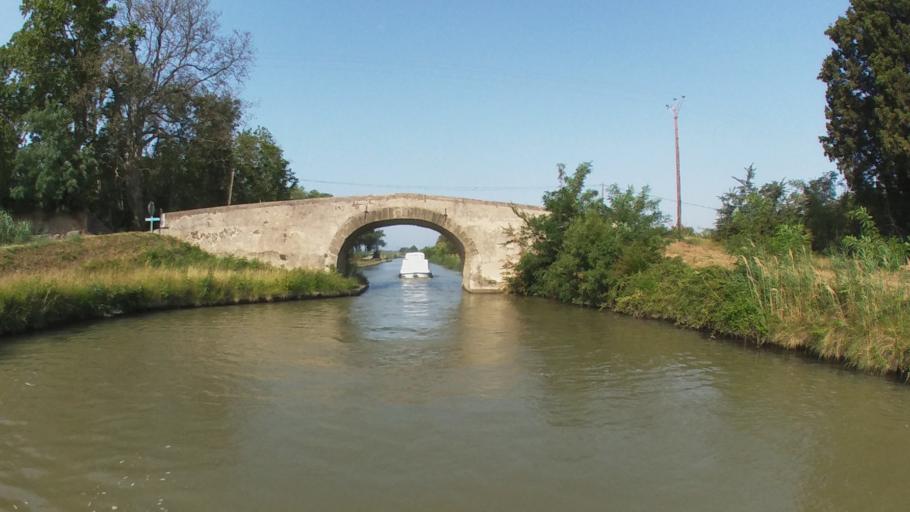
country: FR
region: Languedoc-Roussillon
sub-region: Departement de l'Herault
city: Olonzac
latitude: 43.2651
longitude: 2.6988
